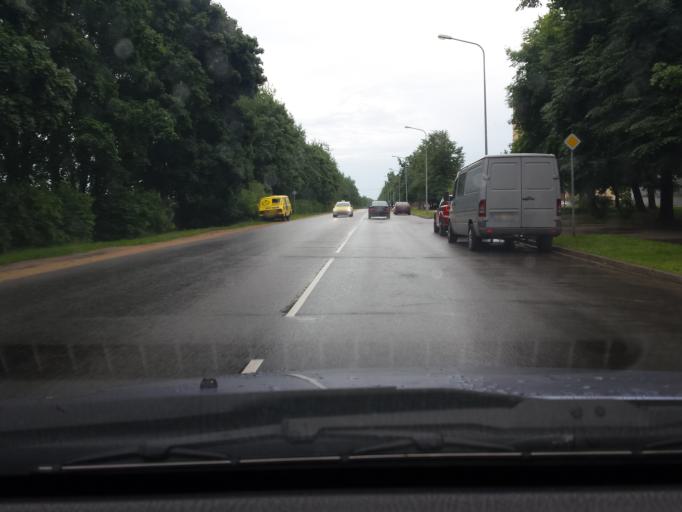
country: LV
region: Kekava
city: Kekava
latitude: 56.9093
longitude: 24.2009
